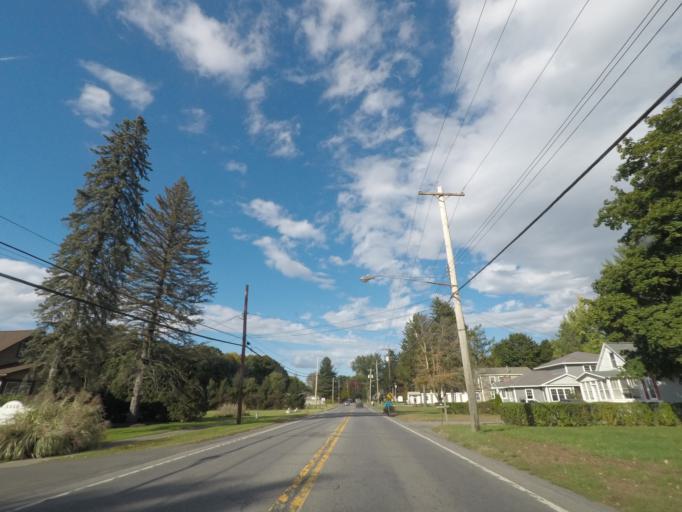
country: US
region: New York
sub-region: Schenectady County
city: Rotterdam
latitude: 42.7473
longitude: -73.9421
